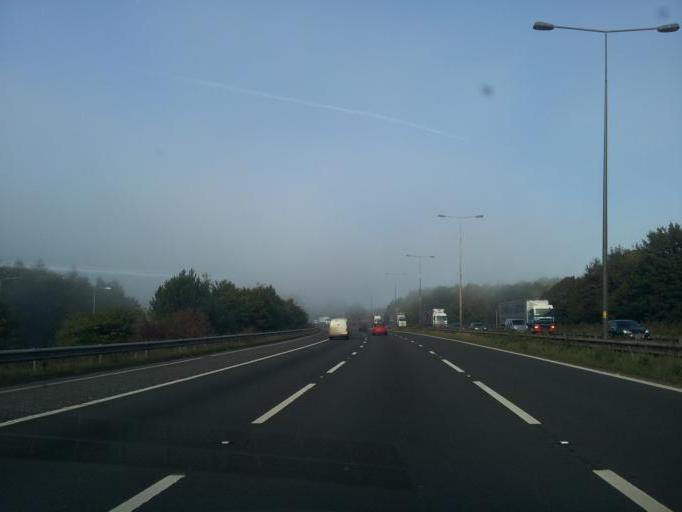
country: GB
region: England
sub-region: City and Borough of Leeds
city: Gildersome
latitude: 53.7473
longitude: -1.6353
